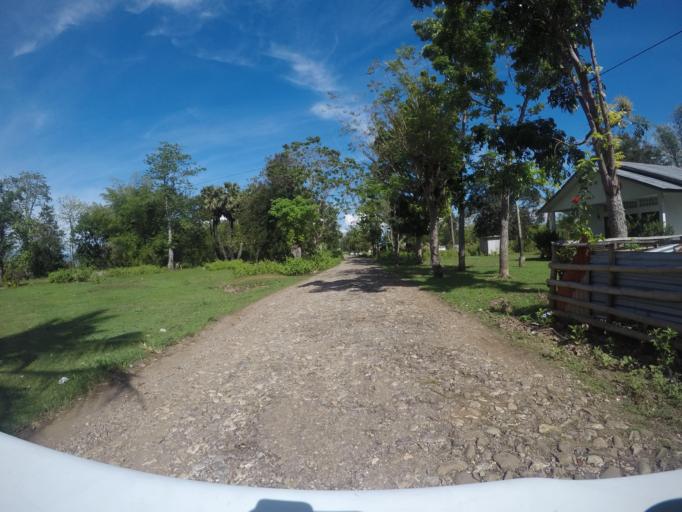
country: TL
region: Bobonaro
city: Maliana
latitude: -8.9873
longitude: 125.1961
